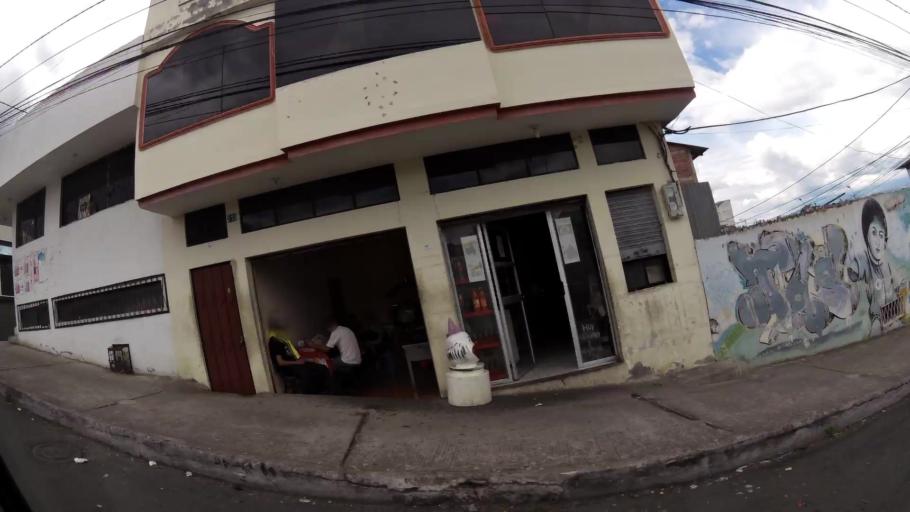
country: EC
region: Tungurahua
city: Ambato
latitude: -1.2502
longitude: -78.6213
